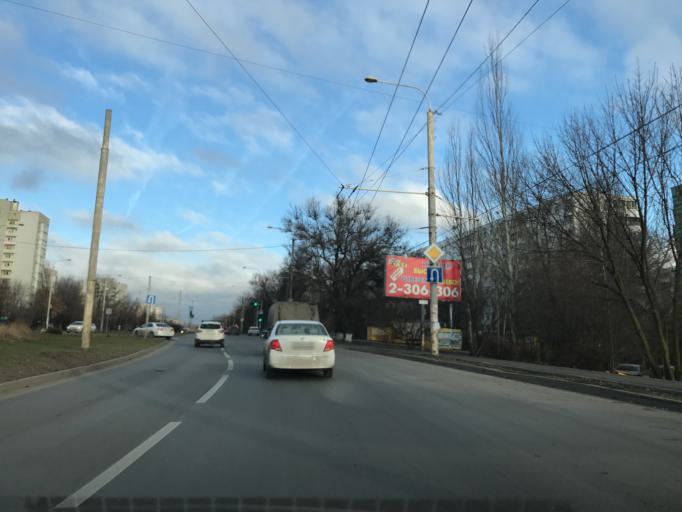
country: RU
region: Rostov
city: Severnyy
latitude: 47.2569
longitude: 39.6427
